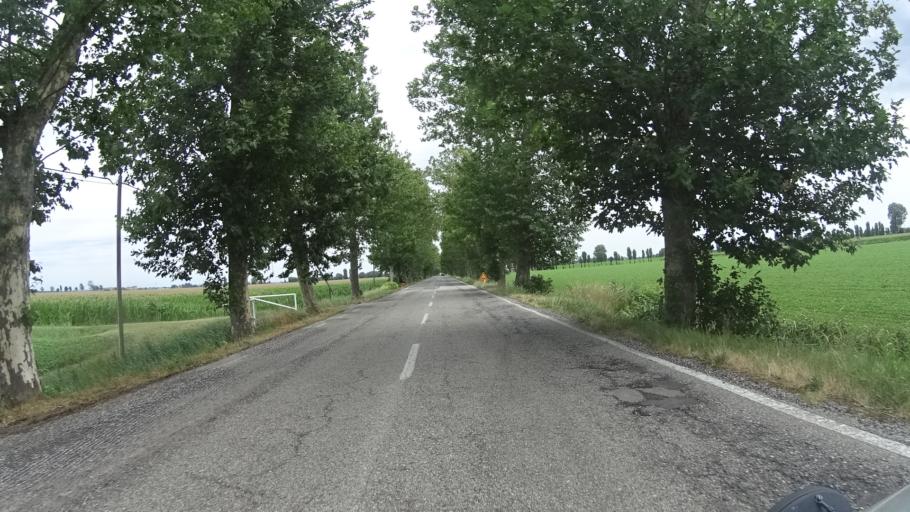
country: IT
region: Veneto
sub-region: Provincia di Venezia
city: Lugugnana
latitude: 45.7233
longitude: 12.9203
